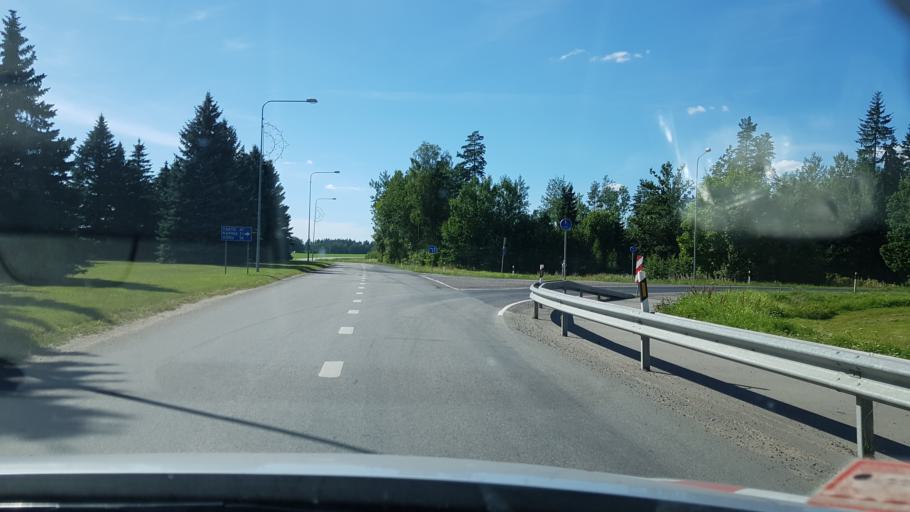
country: EE
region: Polvamaa
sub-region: Polva linn
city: Polva
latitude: 58.0530
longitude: 27.0426
